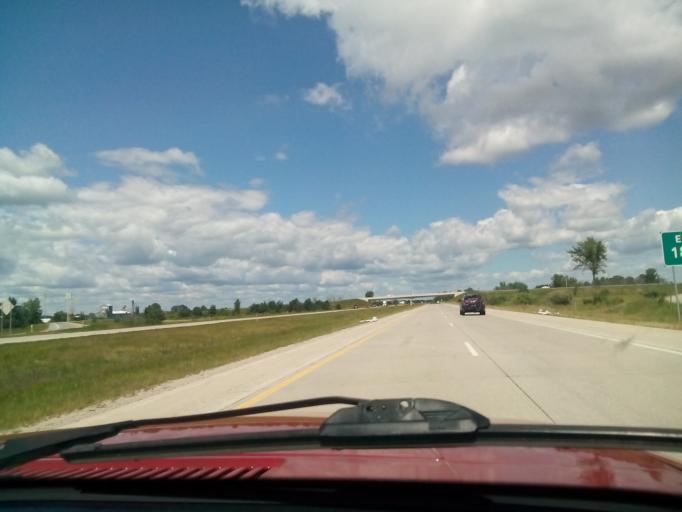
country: US
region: Michigan
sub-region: Bay County
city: Pinconning
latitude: 43.8500
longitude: -84.0204
